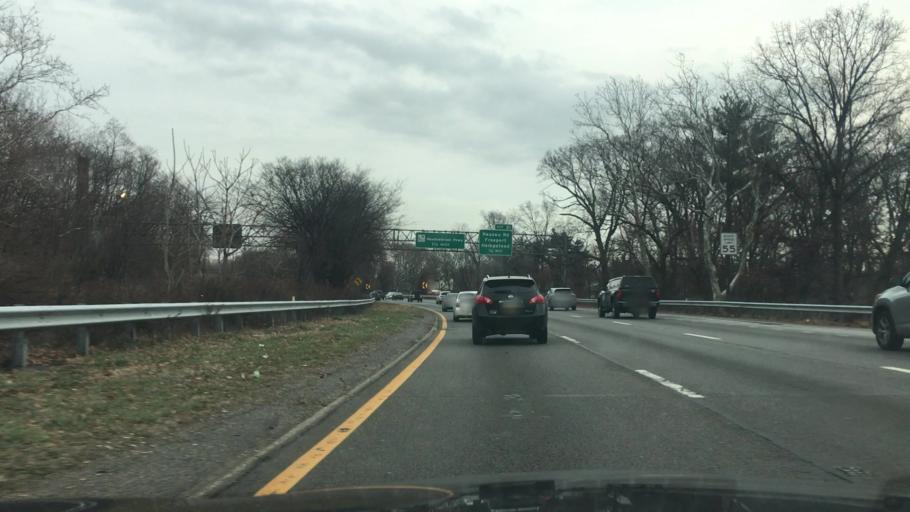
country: US
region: New York
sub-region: Nassau County
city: South Hempstead
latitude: 40.6846
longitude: -73.6107
